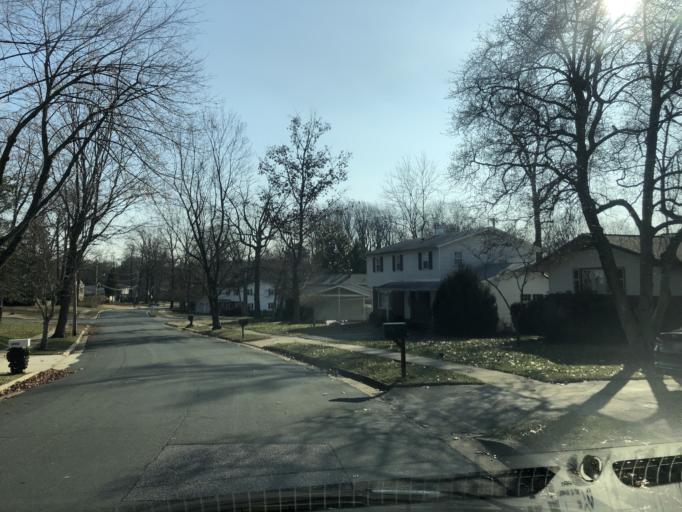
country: US
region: Maryland
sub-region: Anne Arundel County
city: Odenton
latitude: 39.0724
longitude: -76.6931
